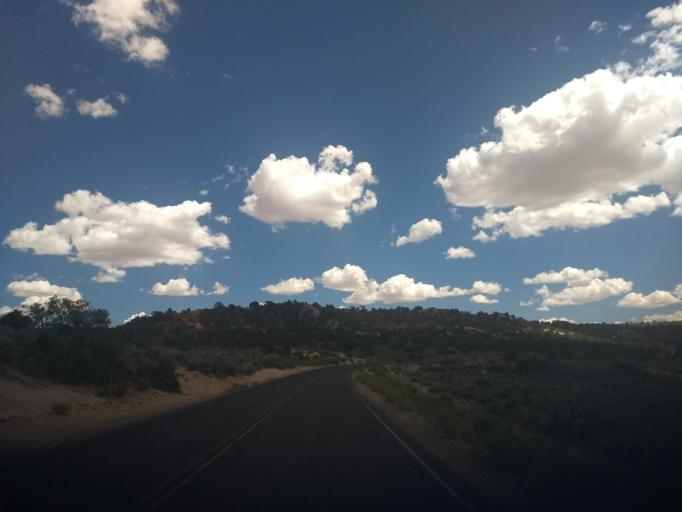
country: US
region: Utah
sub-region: Kane County
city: Kanab
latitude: 37.1215
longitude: -112.6773
